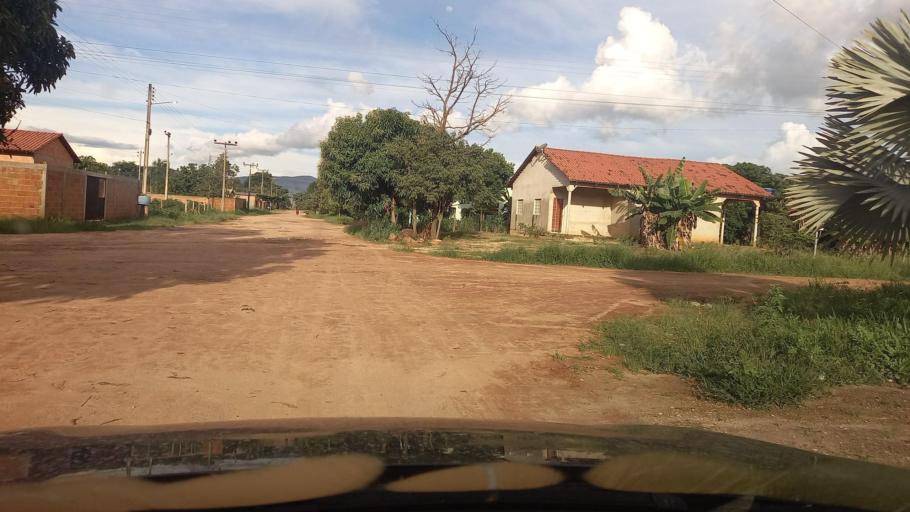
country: BR
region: Goias
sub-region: Cavalcante
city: Cavalcante
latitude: -13.7999
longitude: -47.4432
